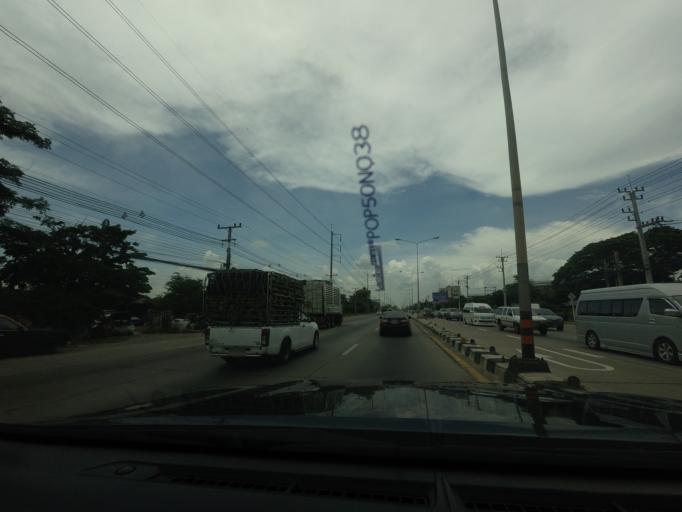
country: TH
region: Nakhon Pathom
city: Nakhon Pathom
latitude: 13.8454
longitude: 100.0240
